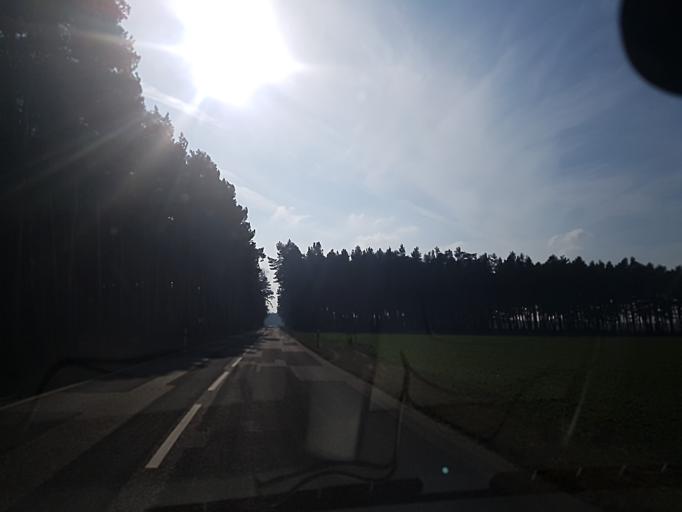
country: DE
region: Brandenburg
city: Wenzlow
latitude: 52.3123
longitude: 12.4410
